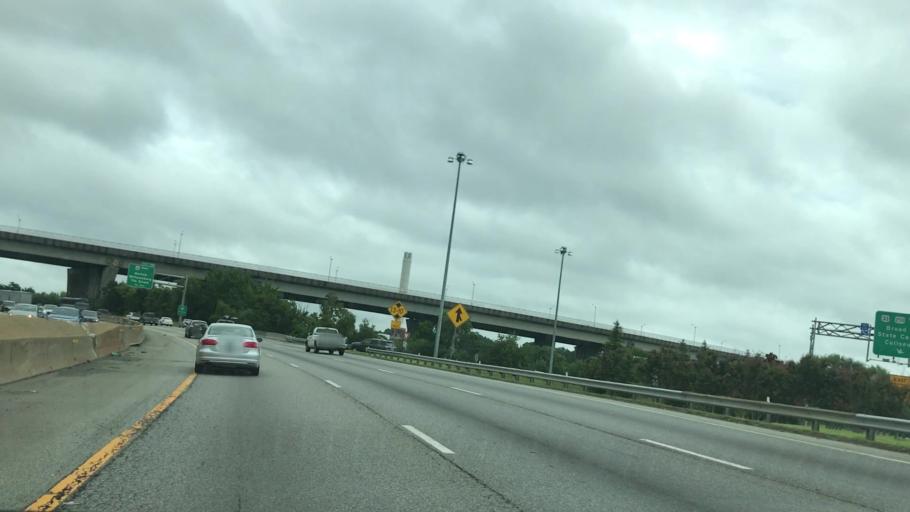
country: US
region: Virginia
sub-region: City of Richmond
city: Richmond
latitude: 37.5390
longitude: -77.4271
